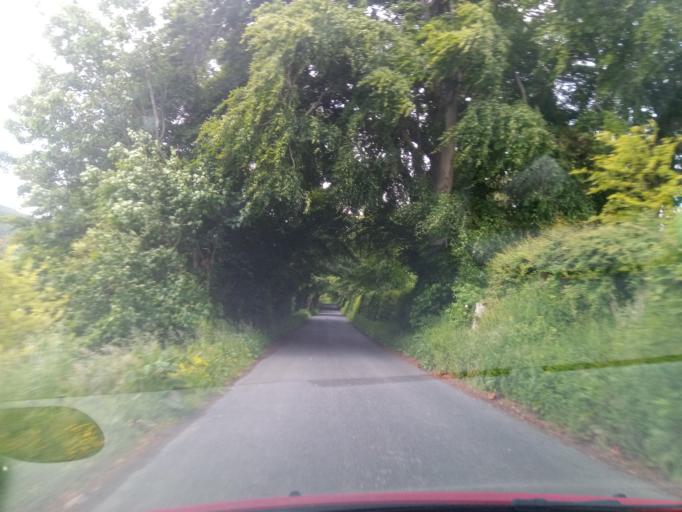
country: GB
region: Scotland
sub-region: The Scottish Borders
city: Selkirk
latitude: 55.5858
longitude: -2.8442
